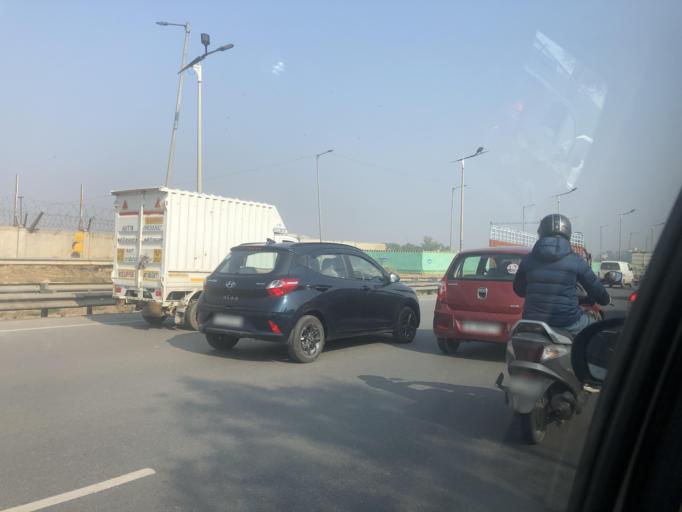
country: IN
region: Haryana
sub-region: Gurgaon
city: Gurgaon
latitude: 28.5362
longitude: 77.1129
